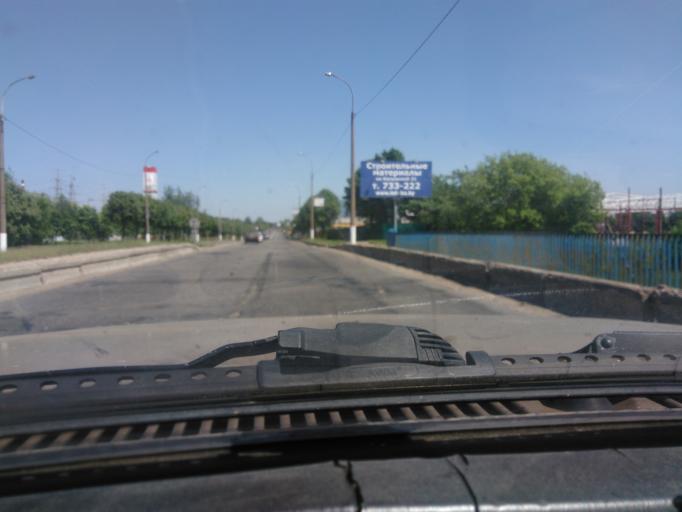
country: BY
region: Mogilev
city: Mahilyow
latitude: 53.9137
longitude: 30.3675
